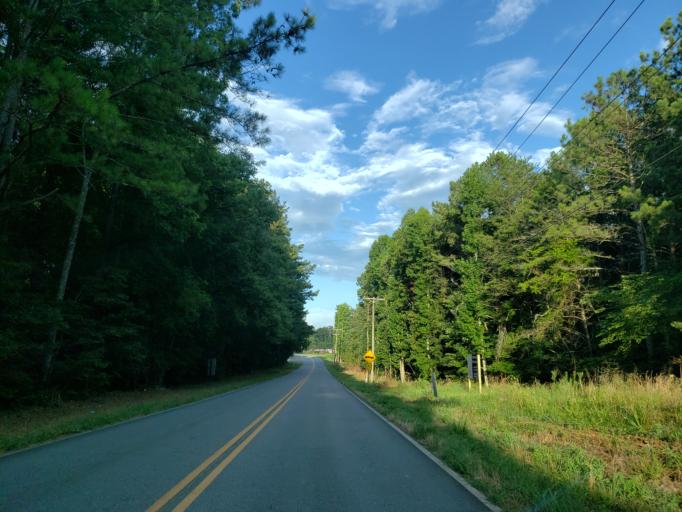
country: US
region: Georgia
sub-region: Cherokee County
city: Canton
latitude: 34.3304
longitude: -84.4930
